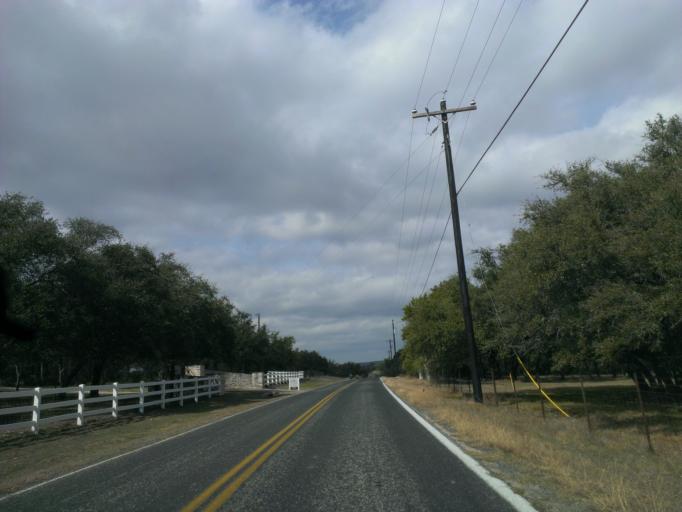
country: US
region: Texas
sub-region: Travis County
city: Briarcliff
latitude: 30.3828
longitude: -98.0967
